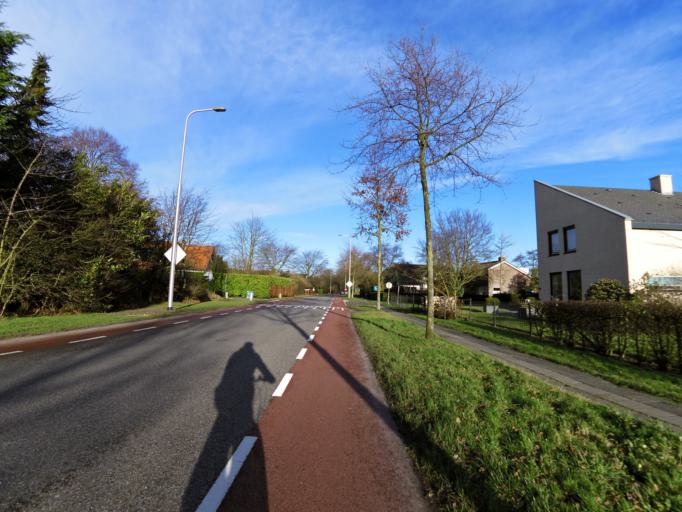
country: NL
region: South Holland
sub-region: Gemeente Hellevoetsluis
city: Nieuwenhoorn
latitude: 51.8989
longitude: 4.0916
